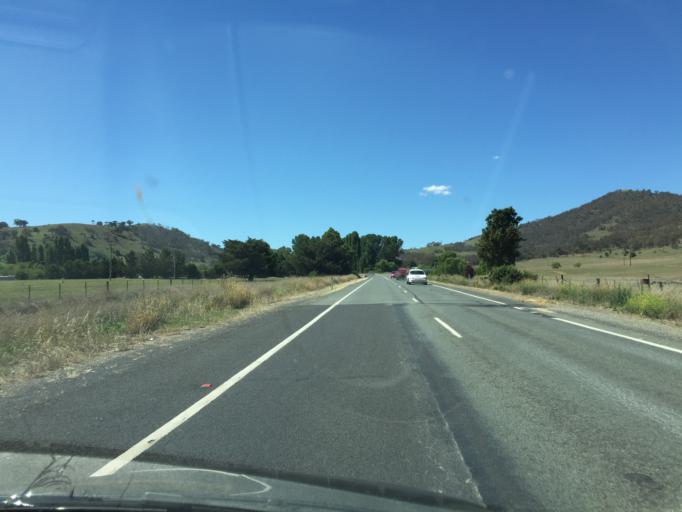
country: AU
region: Australian Capital Territory
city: Macarthur
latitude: -35.6893
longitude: 149.1638
